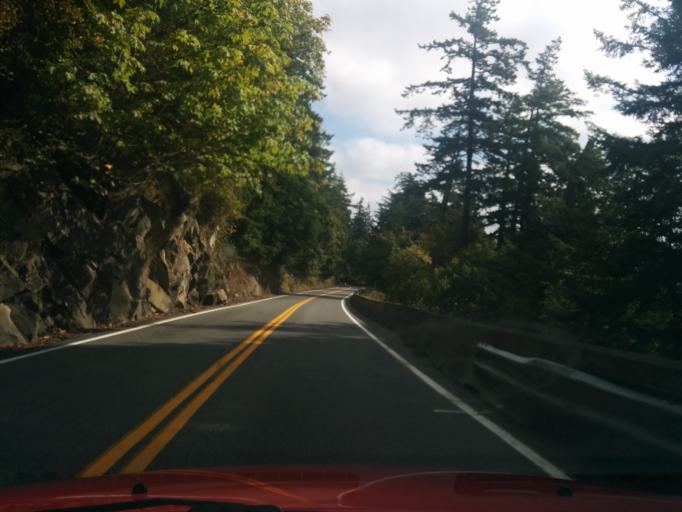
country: US
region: Washington
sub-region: Whatcom County
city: Bellingham
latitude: 48.6286
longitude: -122.4656
